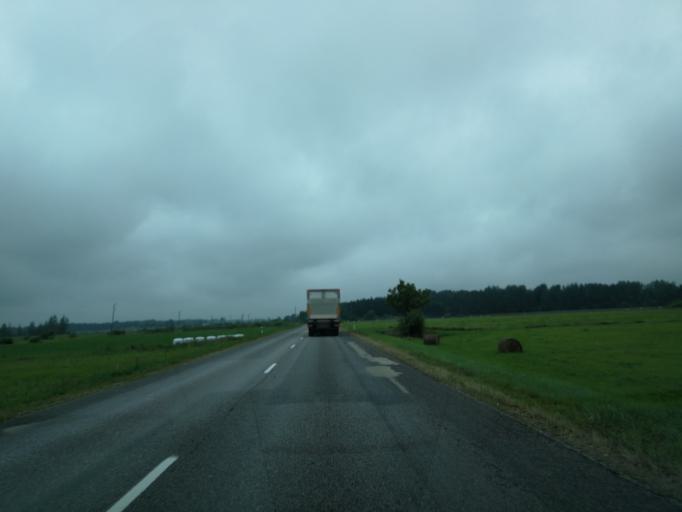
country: LV
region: Livani
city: Livani
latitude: 56.3480
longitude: 26.2747
